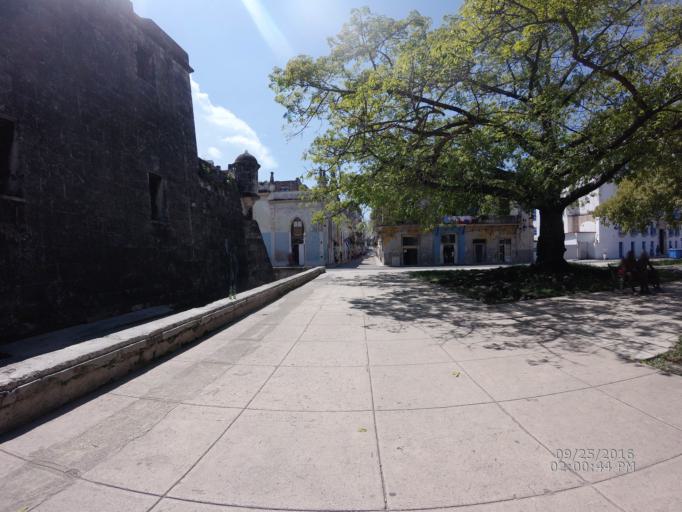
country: CU
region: La Habana
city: Centro Habana
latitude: 23.1426
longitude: -82.3534
